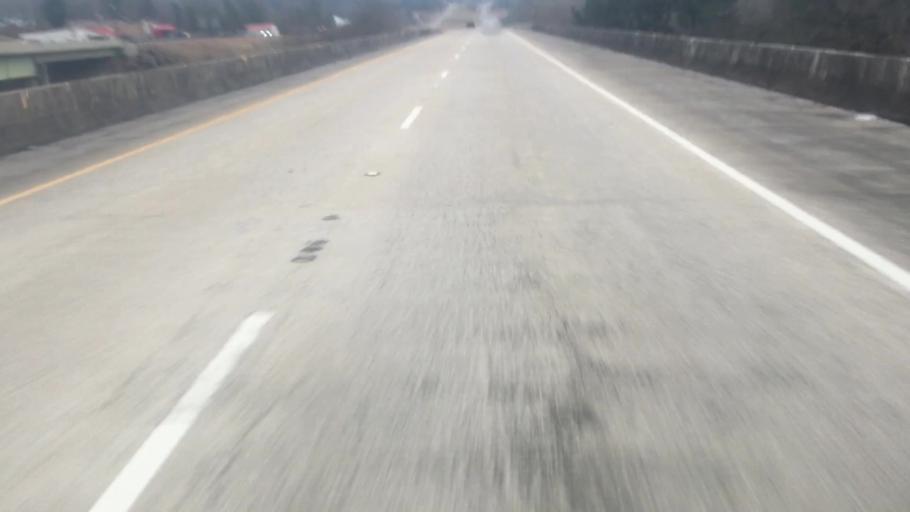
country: US
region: Alabama
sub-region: Walker County
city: Cordova
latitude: 33.8066
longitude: -87.1405
